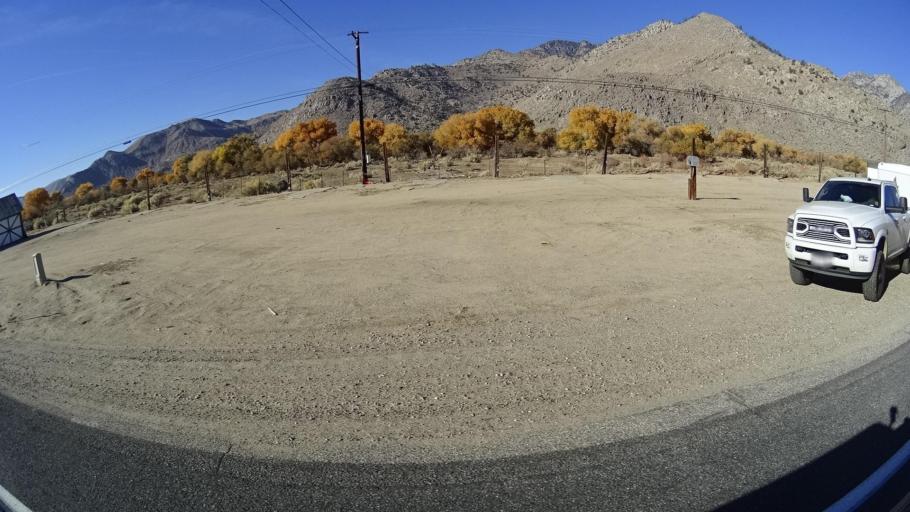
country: US
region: California
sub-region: Kern County
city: Weldon
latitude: 35.6875
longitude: -118.2363
